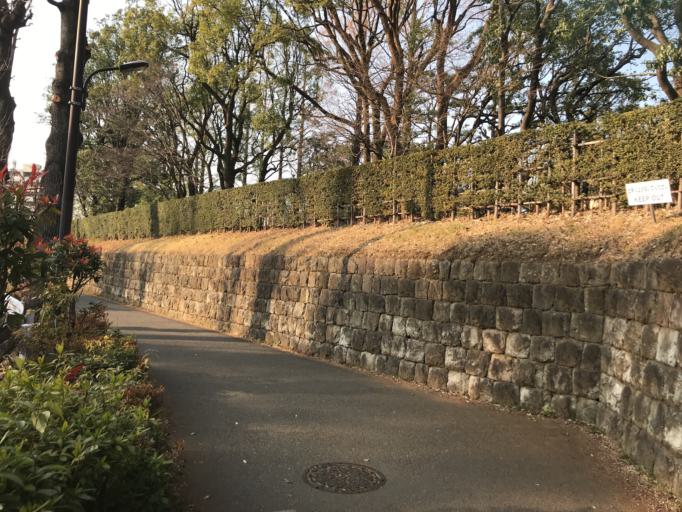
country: JP
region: Tokyo
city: Tokyo
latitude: 35.6744
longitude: 139.7233
